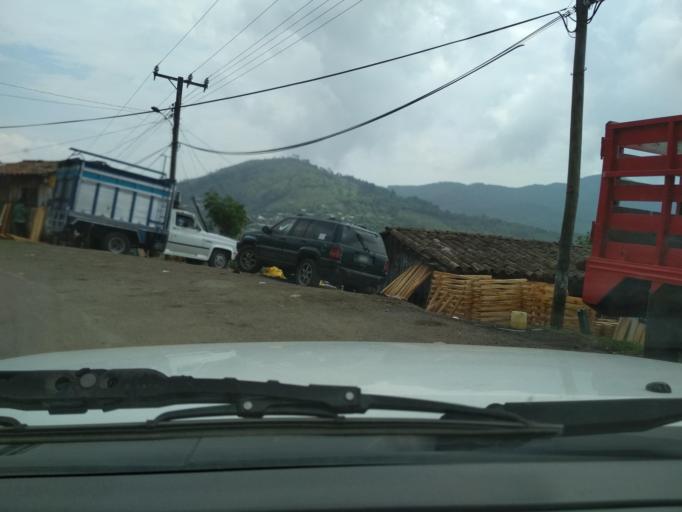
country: MX
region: Veracruz
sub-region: Camerino Z. Mendoza
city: Necoxtla
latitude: 18.7738
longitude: -97.1530
